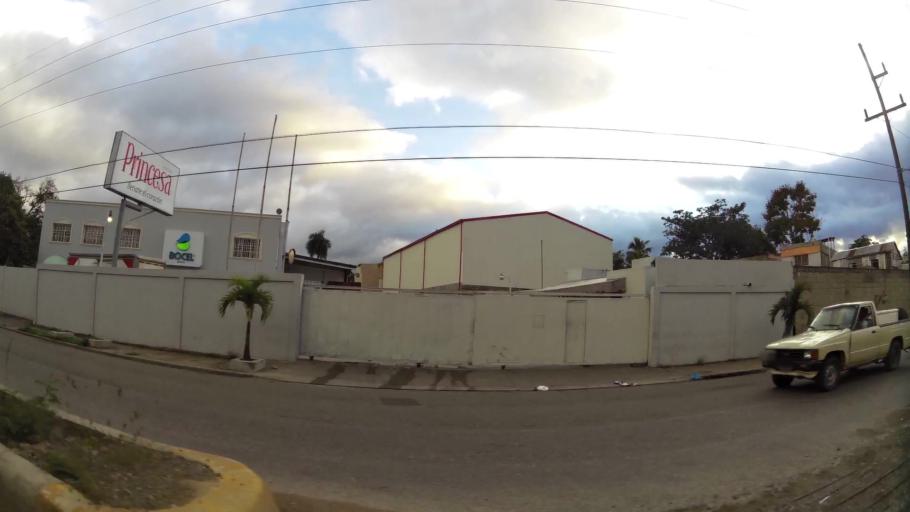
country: DO
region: Santo Domingo
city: Santo Domingo Oeste
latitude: 18.5076
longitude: -69.9947
